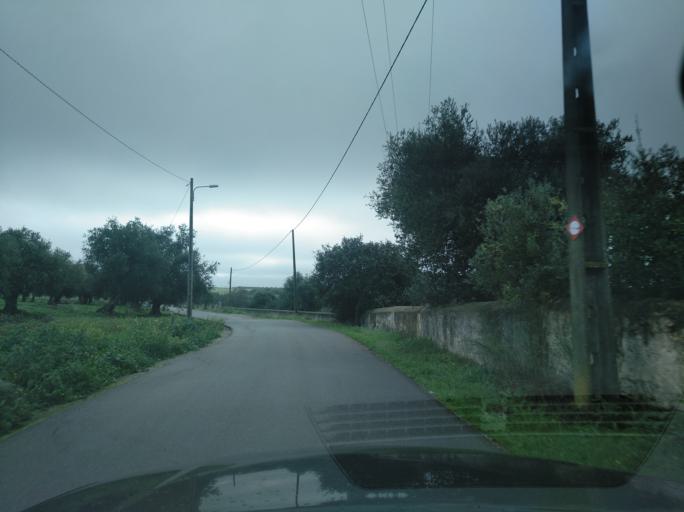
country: PT
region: Portalegre
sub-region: Elvas
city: Elvas
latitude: 38.8648
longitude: -7.1659
